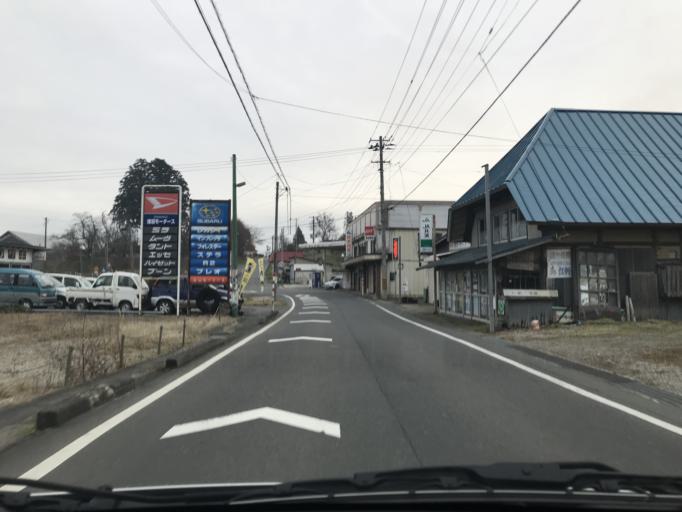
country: JP
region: Iwate
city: Kitakami
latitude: 39.2842
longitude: 141.2624
